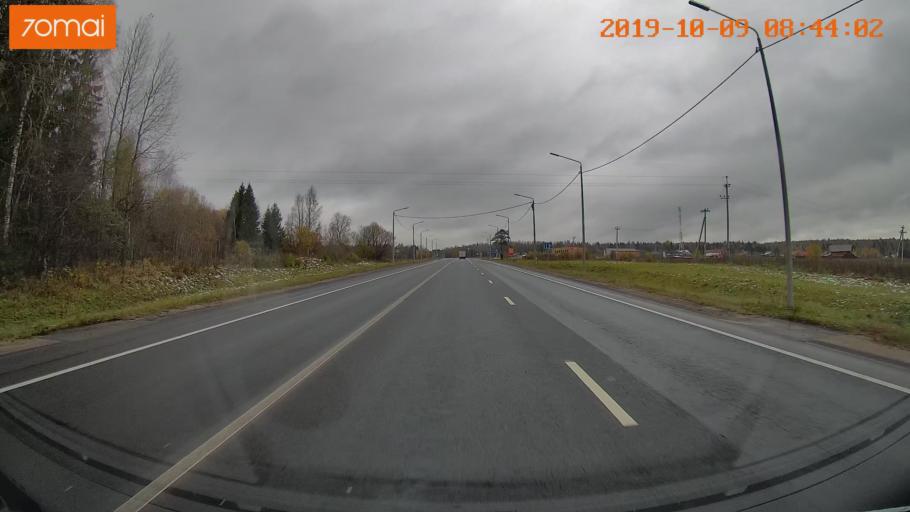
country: RU
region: Vologda
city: Gryazovets
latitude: 59.0309
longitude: 40.1110
